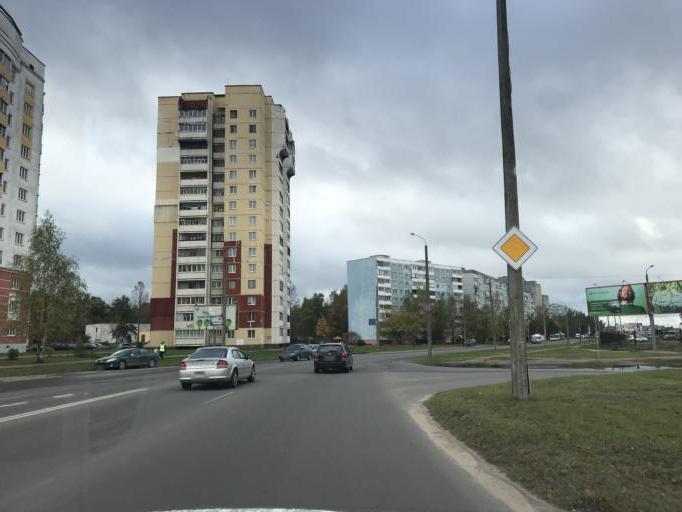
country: BY
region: Mogilev
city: Mahilyow
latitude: 53.8796
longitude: 30.3692
